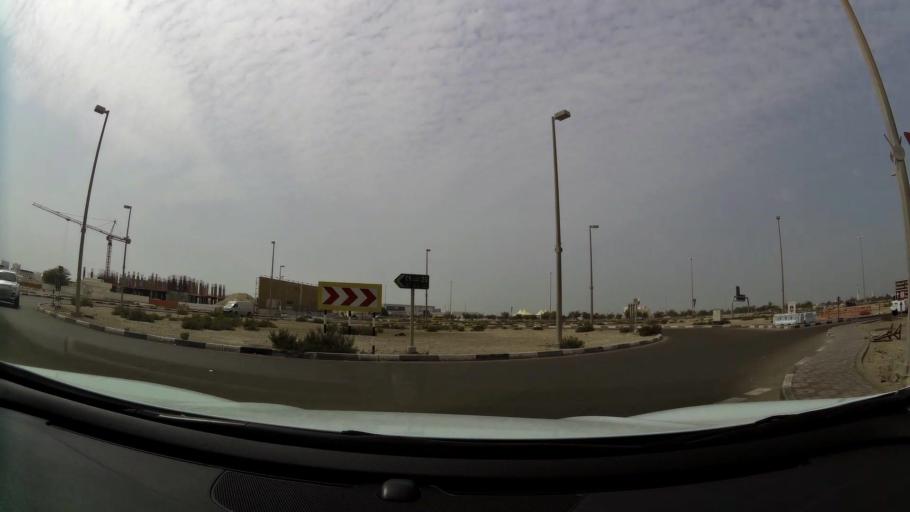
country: AE
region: Abu Dhabi
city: Abu Dhabi
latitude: 24.5358
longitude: 54.6858
